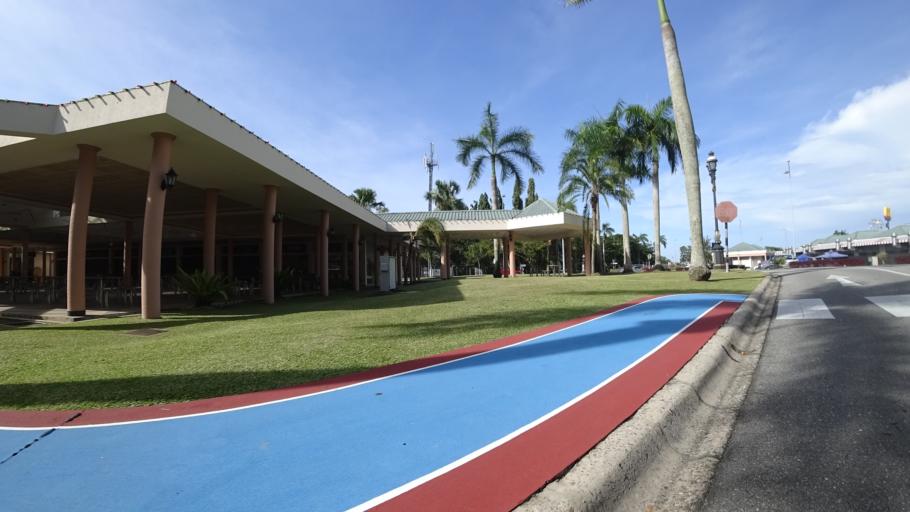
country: BN
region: Brunei and Muara
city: Bandar Seri Begawan
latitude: 4.9366
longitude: 114.8329
